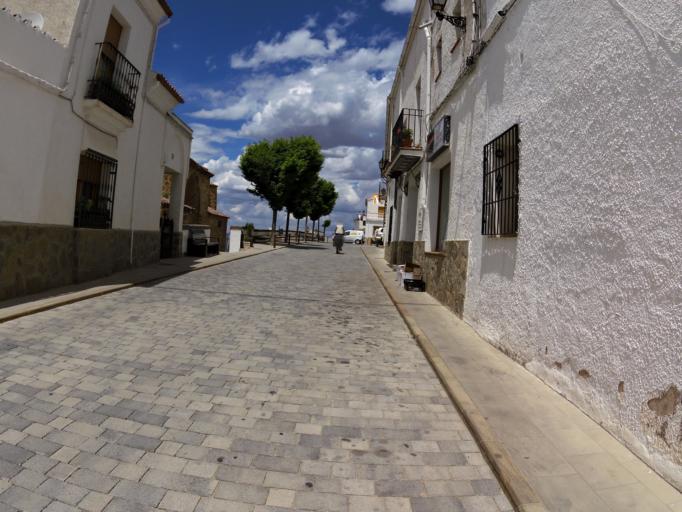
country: ES
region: Andalusia
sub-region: Provincia de Jaen
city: Segura de la Sierra
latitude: 38.2980
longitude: -2.6518
